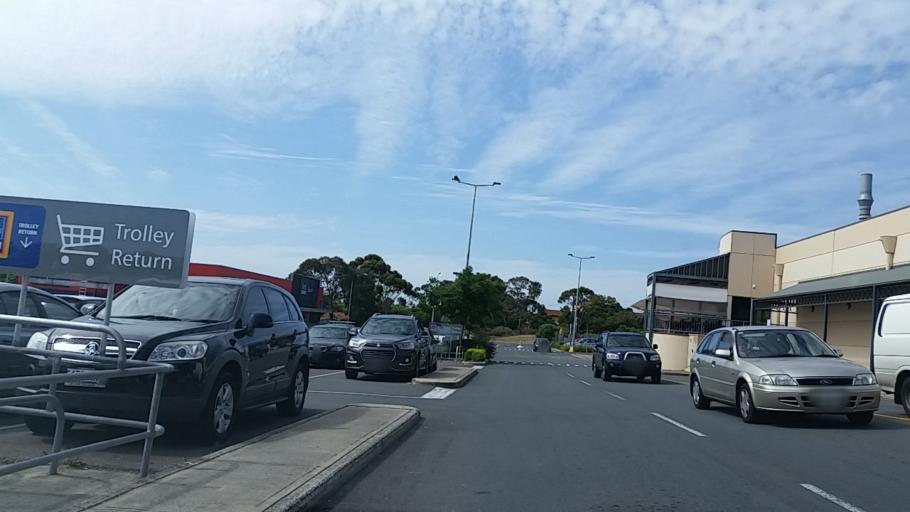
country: AU
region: South Australia
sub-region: Salisbury
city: Ingle Farm
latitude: -34.8290
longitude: 138.6479
